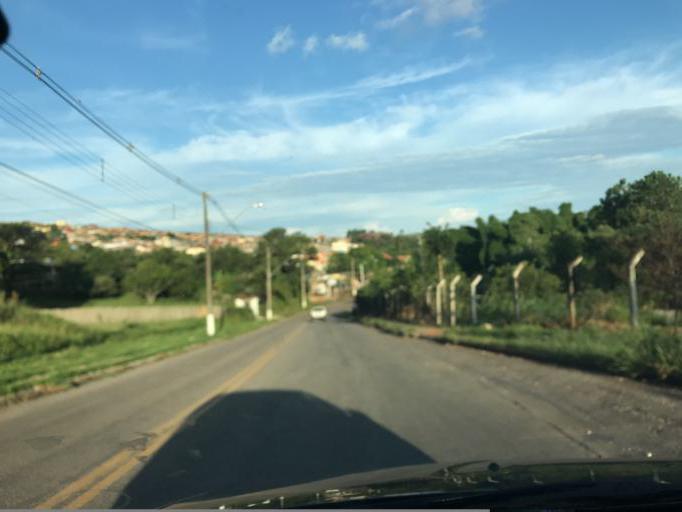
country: BR
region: Minas Gerais
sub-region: Tres Coracoes
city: Tres Coracoes
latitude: -21.6965
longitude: -45.2454
